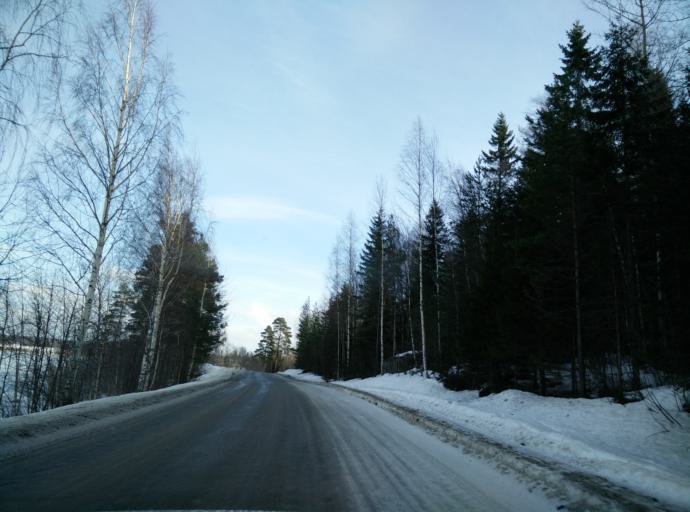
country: SE
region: Vaesternorrland
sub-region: Sundsvalls Kommun
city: Njurundabommen
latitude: 62.2216
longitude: 17.3259
